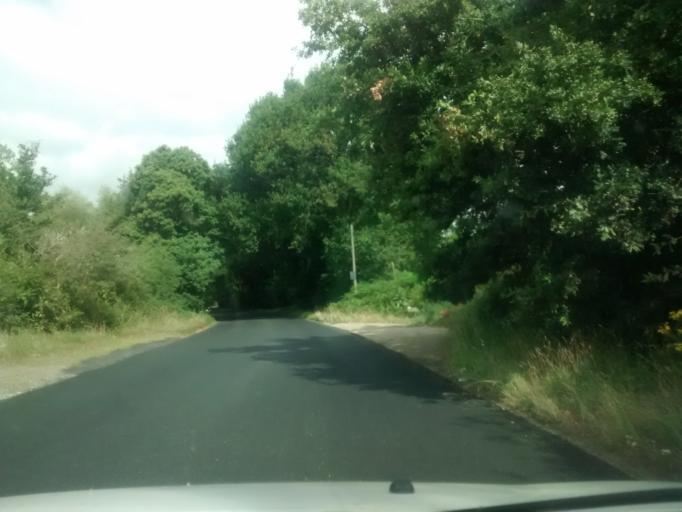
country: FR
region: Brittany
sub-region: Departement d'Ille-et-Vilaine
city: Saint-Jacques-de-la-Lande
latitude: 48.0855
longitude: -1.7319
